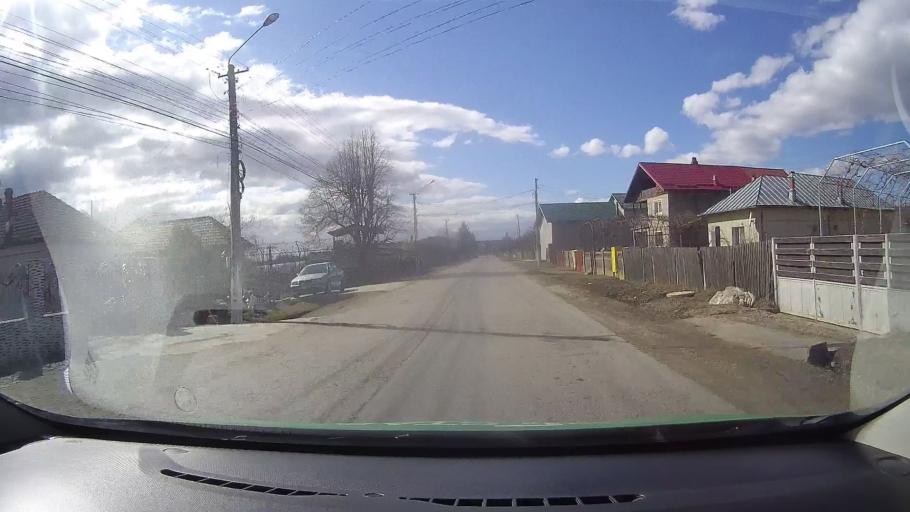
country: RO
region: Dambovita
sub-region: Comuna Vulcana-Pandele
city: Gura Vulcanei
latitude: 45.0243
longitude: 25.4029
